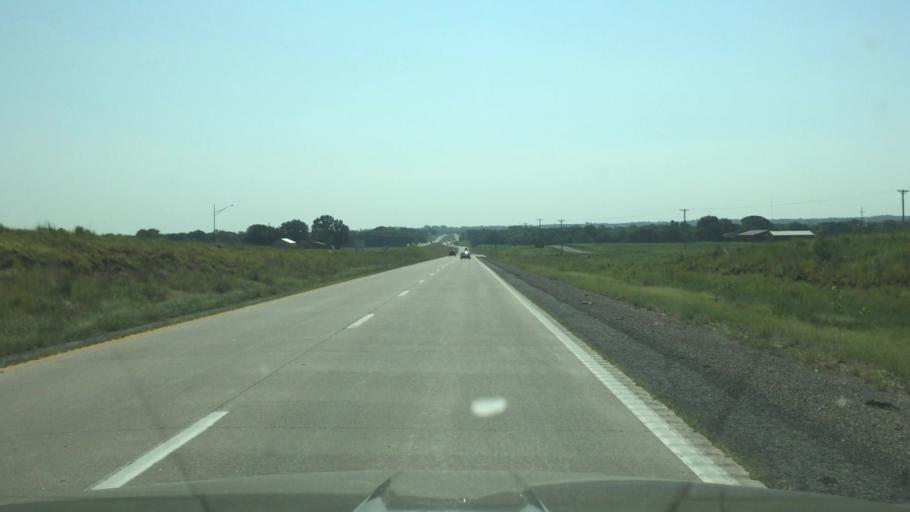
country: US
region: Missouri
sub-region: Johnson County
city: Warrensburg
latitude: 38.7729
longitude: -93.6837
